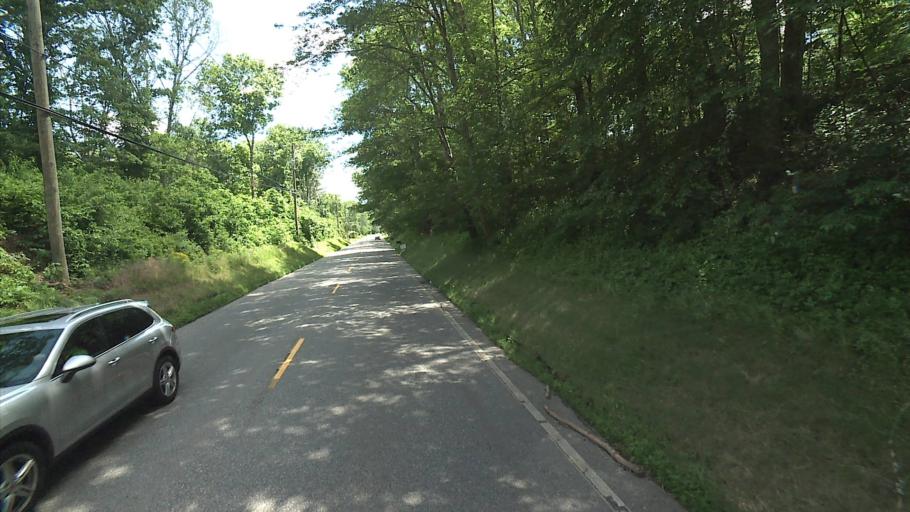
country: US
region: Connecticut
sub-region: New London County
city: Pawcatuck
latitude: 41.4209
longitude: -71.8929
